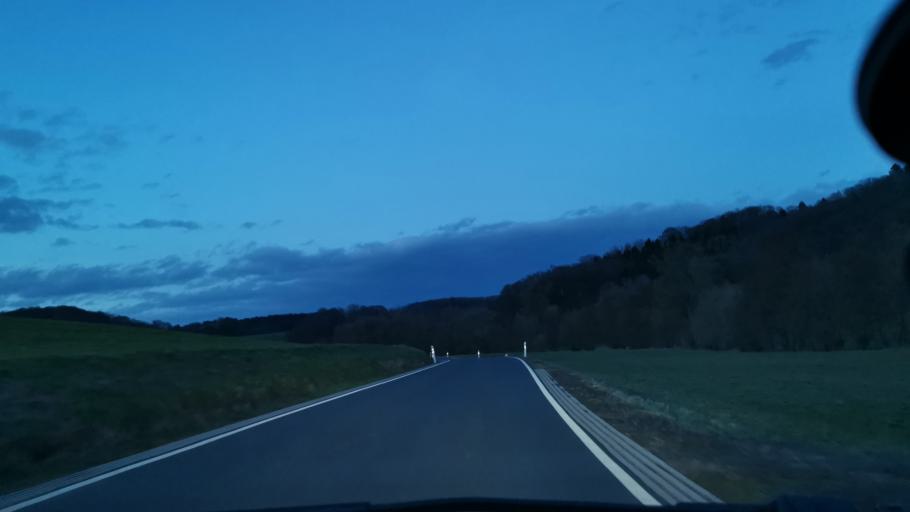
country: DE
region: Hesse
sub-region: Regierungsbezirk Kassel
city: Cornberg
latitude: 51.0593
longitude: 9.8326
